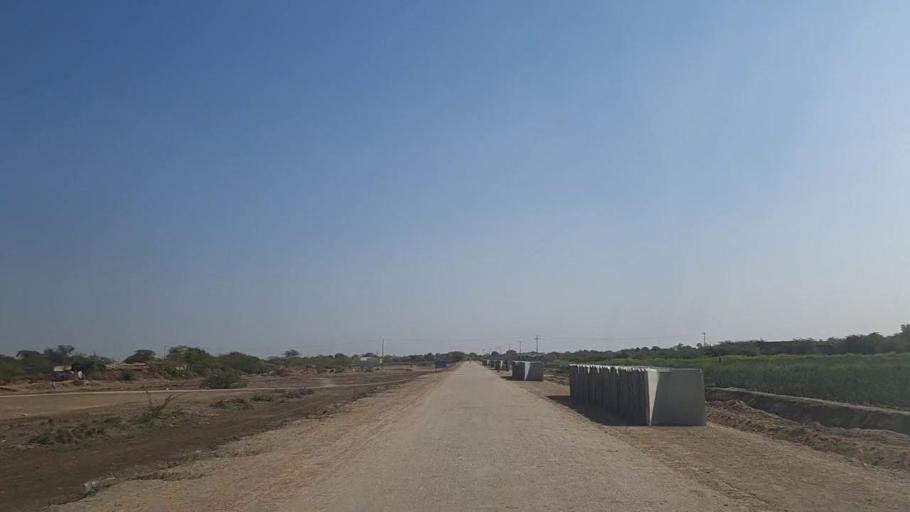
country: PK
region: Sindh
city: Digri
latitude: 25.1605
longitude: 69.1353
